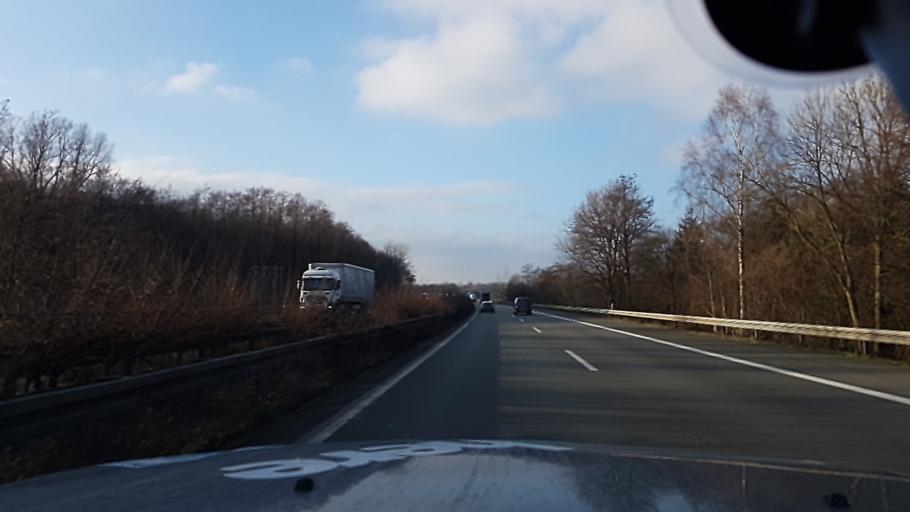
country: DE
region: North Rhine-Westphalia
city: Ibbenburen
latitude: 52.2585
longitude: 7.7672
